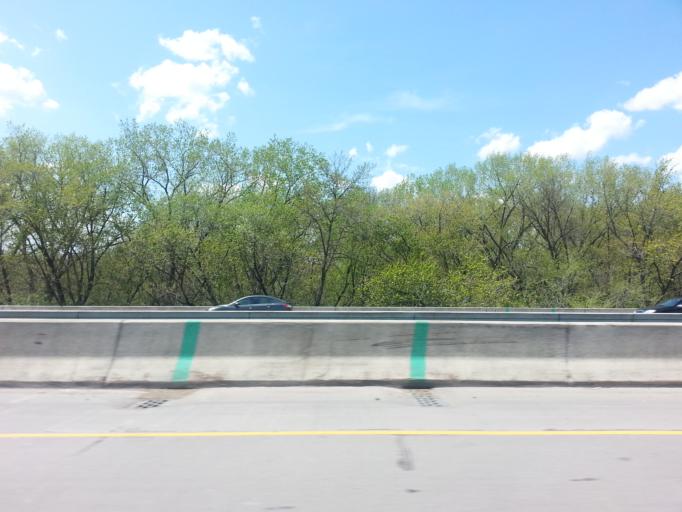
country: US
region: Minnesota
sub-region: Scott County
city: Savage
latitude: 44.8004
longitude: -93.3983
